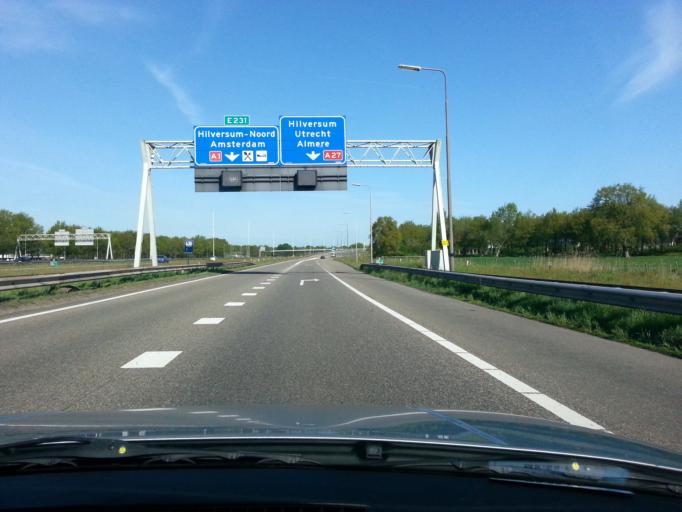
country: NL
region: North Holland
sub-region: Gemeente Laren
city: Laren
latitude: 52.2264
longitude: 5.2518
